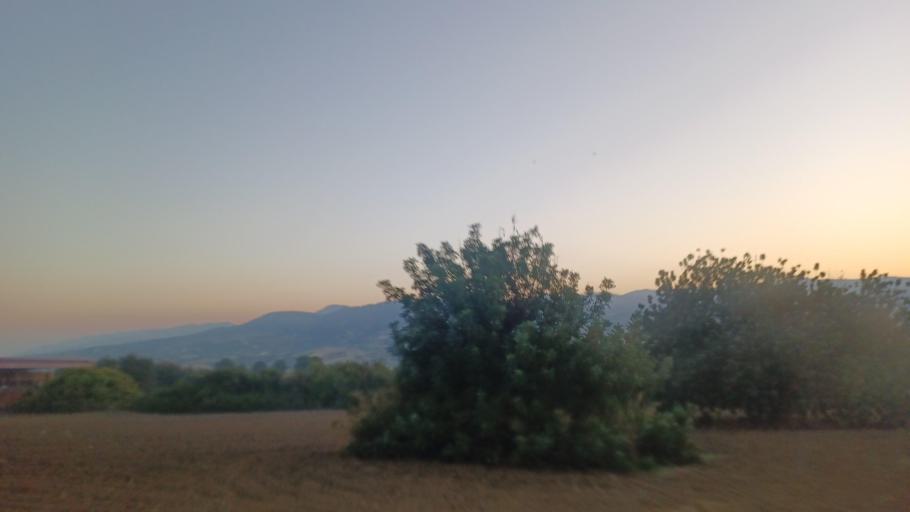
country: CY
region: Pafos
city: Polis
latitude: 34.9832
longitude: 32.4359
